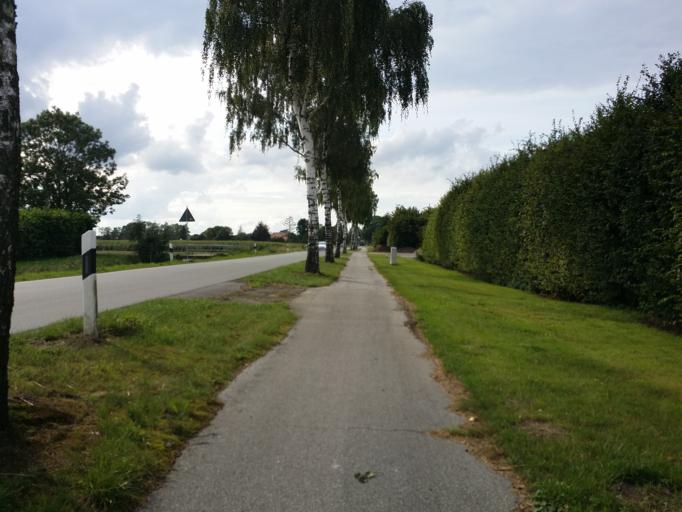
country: DE
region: Lower Saxony
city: Oederquart
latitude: 53.7805
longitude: 9.2647
